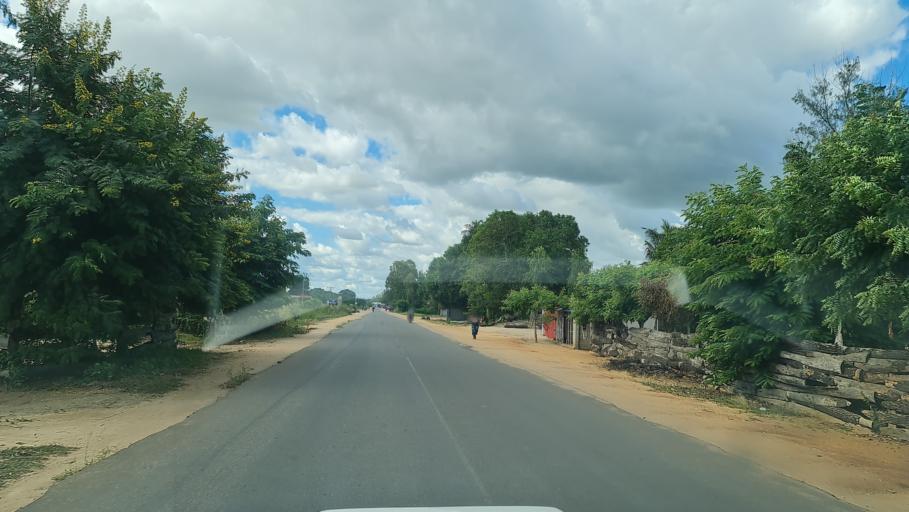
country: MZ
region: Zambezia
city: Quelimane
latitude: -17.5998
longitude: 36.8065
